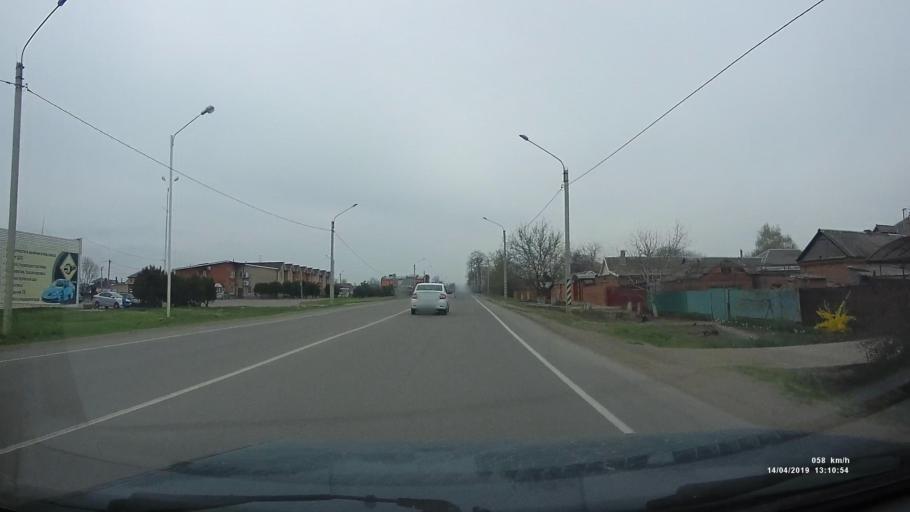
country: RU
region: Rostov
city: Kuleshovka
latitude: 47.1078
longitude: 39.6483
